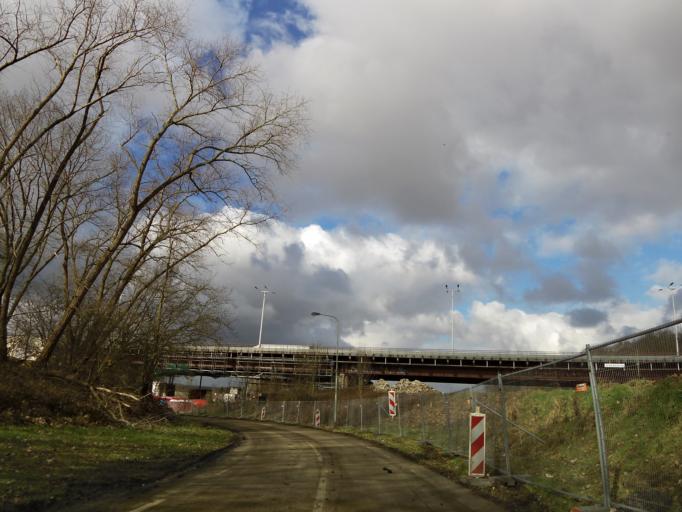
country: NL
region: Limburg
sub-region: Gemeente Stein
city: Stein
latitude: 50.9583
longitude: 5.7570
